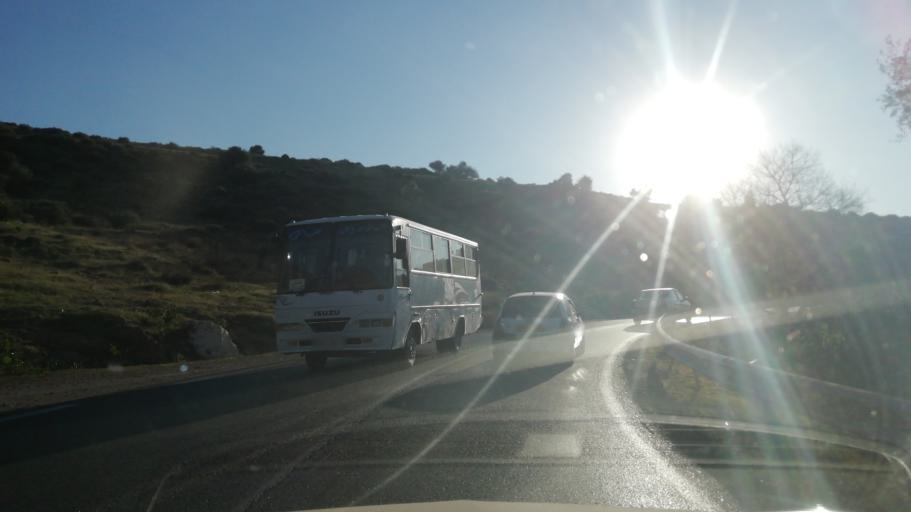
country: DZ
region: Tlemcen
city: Beni Mester
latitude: 34.8532
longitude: -1.4488
